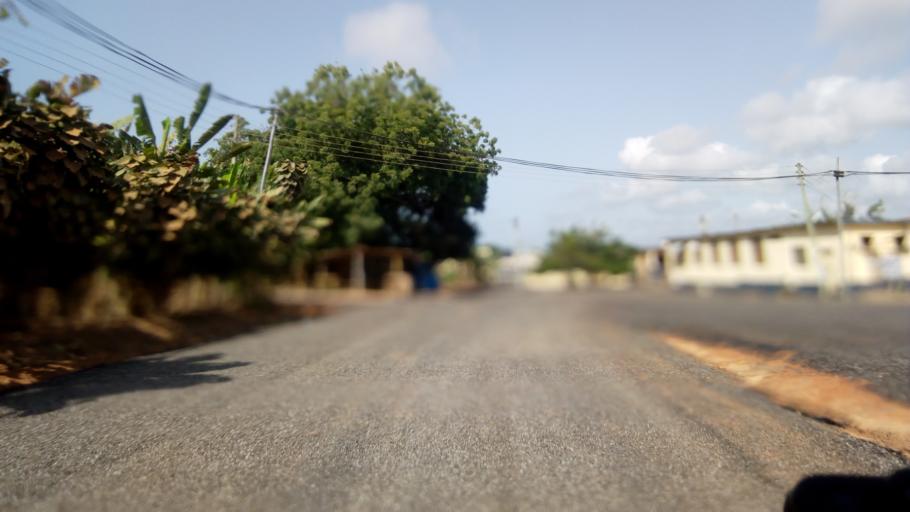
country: GH
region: Central
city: Cape Coast
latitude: 5.1221
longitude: -1.2695
